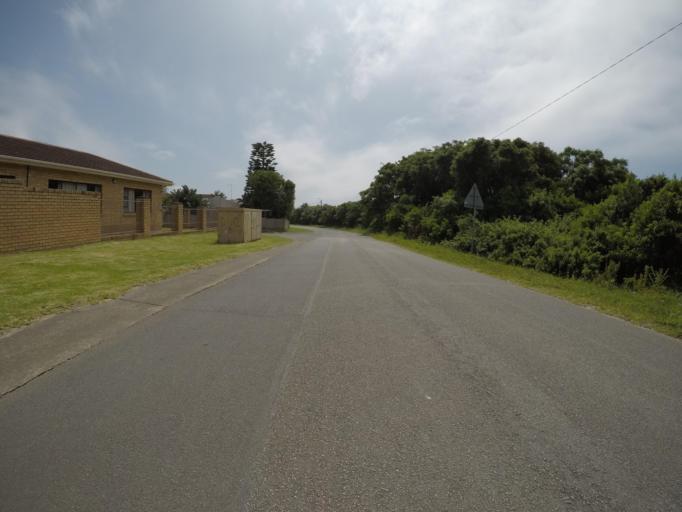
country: ZA
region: Eastern Cape
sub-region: Buffalo City Metropolitan Municipality
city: East London
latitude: -32.9376
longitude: 28.0269
